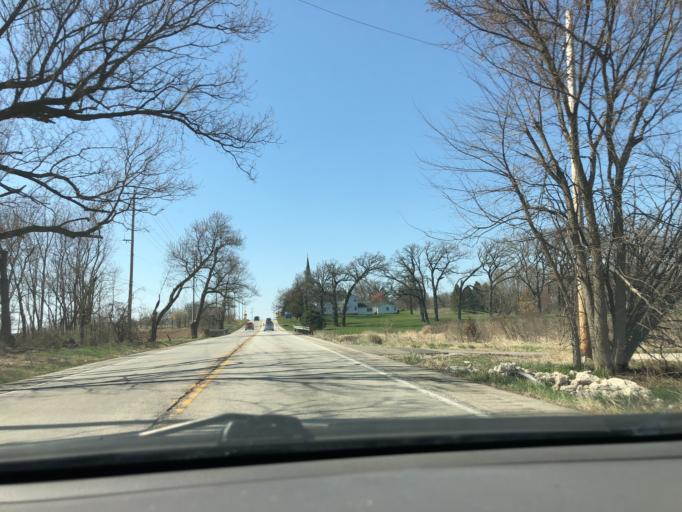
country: US
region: Illinois
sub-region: Kane County
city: Hampshire
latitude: 42.1580
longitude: -88.5232
